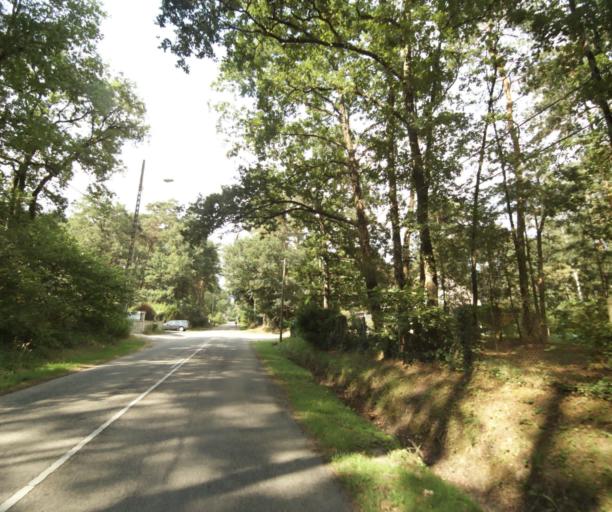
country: FR
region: Ile-de-France
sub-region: Departement de Seine-et-Marne
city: Arbonne-la-Foret
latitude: 48.4039
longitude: 2.5611
